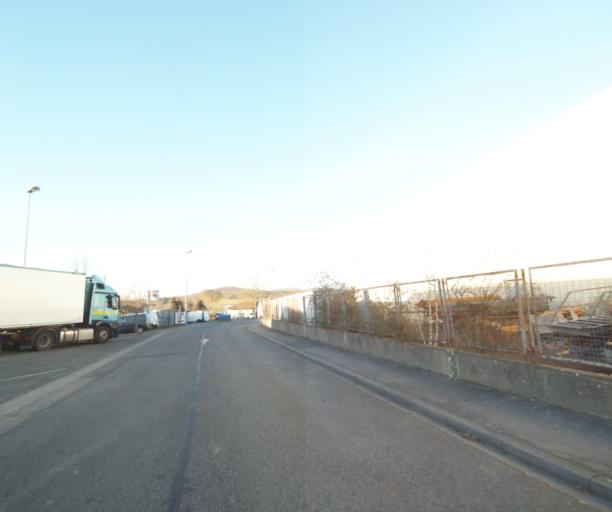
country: FR
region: Lorraine
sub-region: Departement de Meurthe-et-Moselle
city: Pulnoy
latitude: 48.7051
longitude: 6.2525
